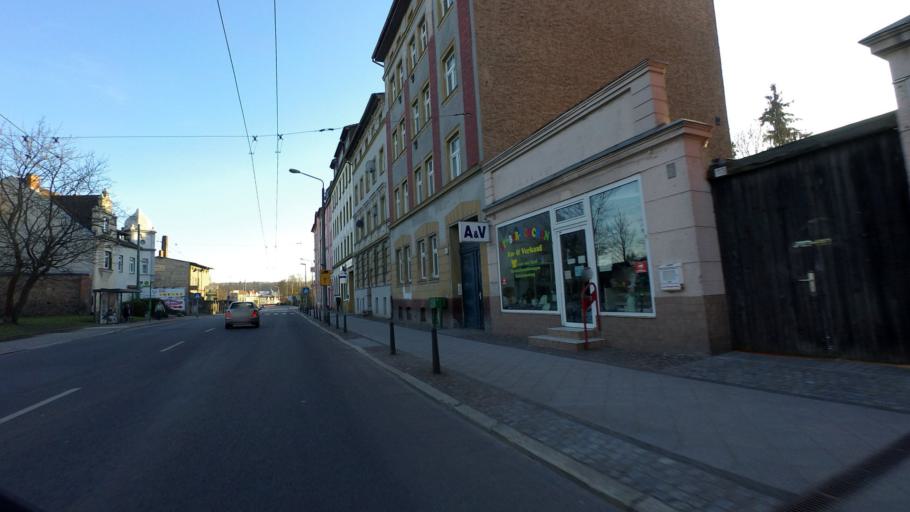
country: DE
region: Brandenburg
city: Eberswalde
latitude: 52.8380
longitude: 13.8197
